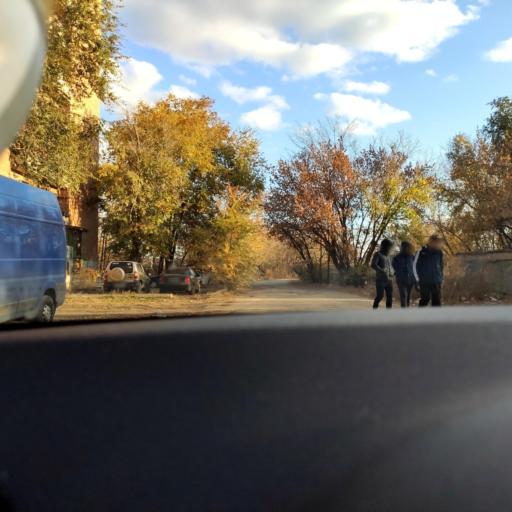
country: RU
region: Samara
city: Samara
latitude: 53.2140
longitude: 50.2661
